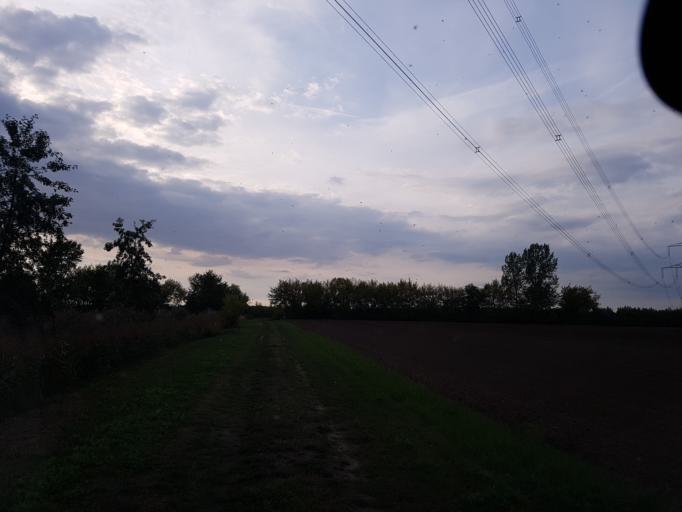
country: DE
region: Brandenburg
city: Bad Liebenwerda
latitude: 51.5494
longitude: 13.4042
